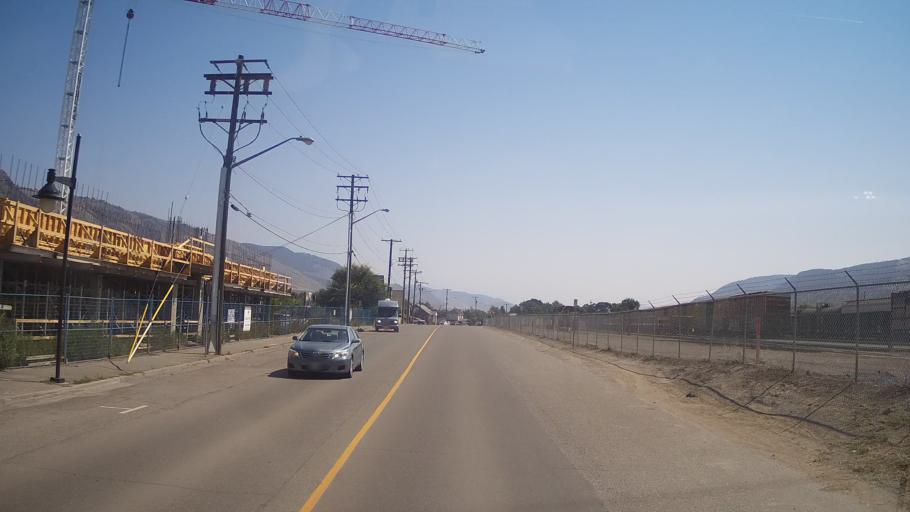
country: CA
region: British Columbia
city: Kamloops
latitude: 50.6783
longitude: -120.3282
